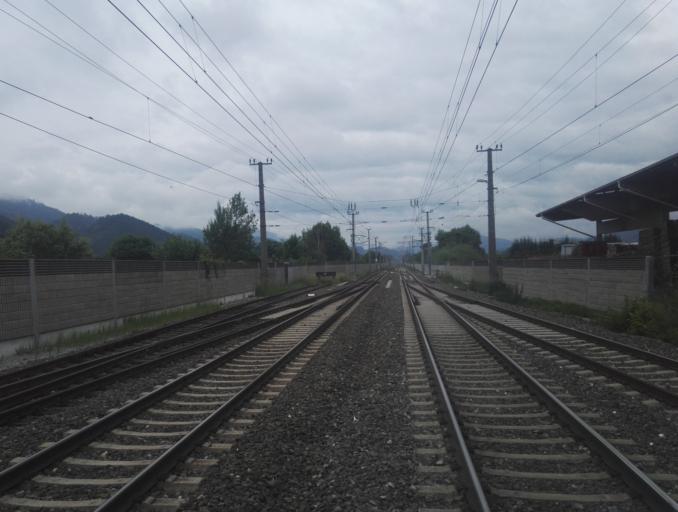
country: AT
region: Styria
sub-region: Politischer Bezirk Bruck-Muerzzuschlag
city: Sankt Marein im Muerztal
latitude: 47.4703
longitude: 15.3660
